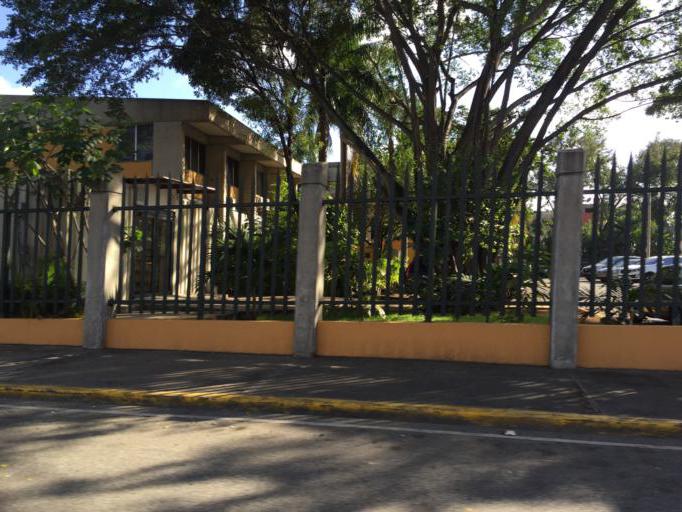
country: DO
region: Nacional
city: Santo Domingo
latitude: 18.4882
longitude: -69.9612
